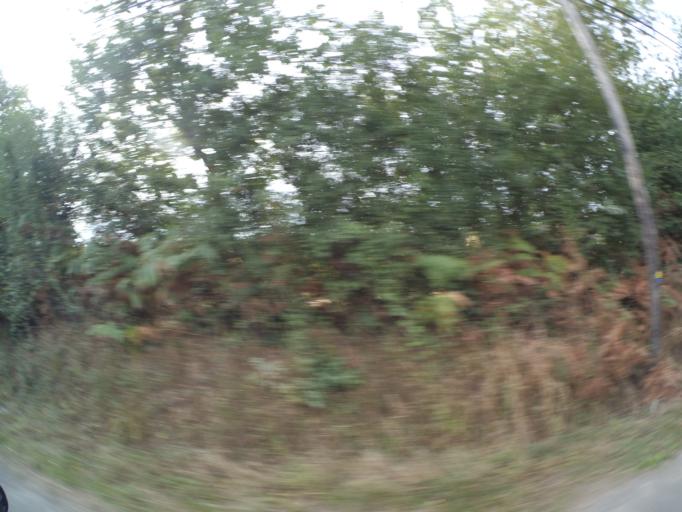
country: FR
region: Pays de la Loire
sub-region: Departement de Maine-et-Loire
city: La Chapelle-du-Genet
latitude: 47.1535
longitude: -1.0260
